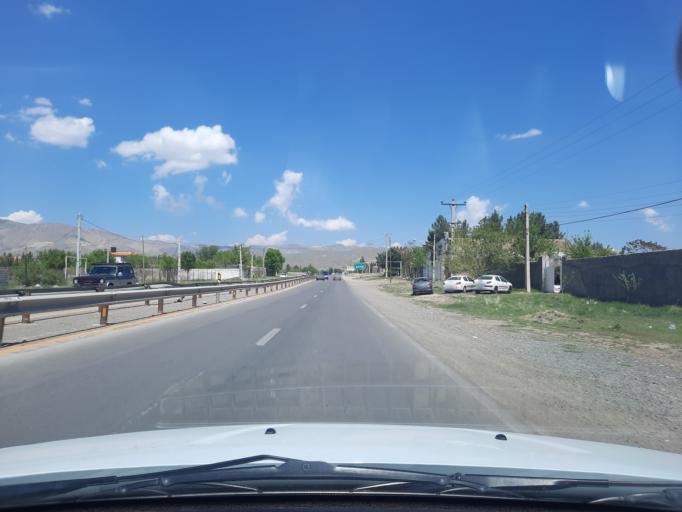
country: IR
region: Qazvin
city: Alvand
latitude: 36.2970
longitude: 50.1392
